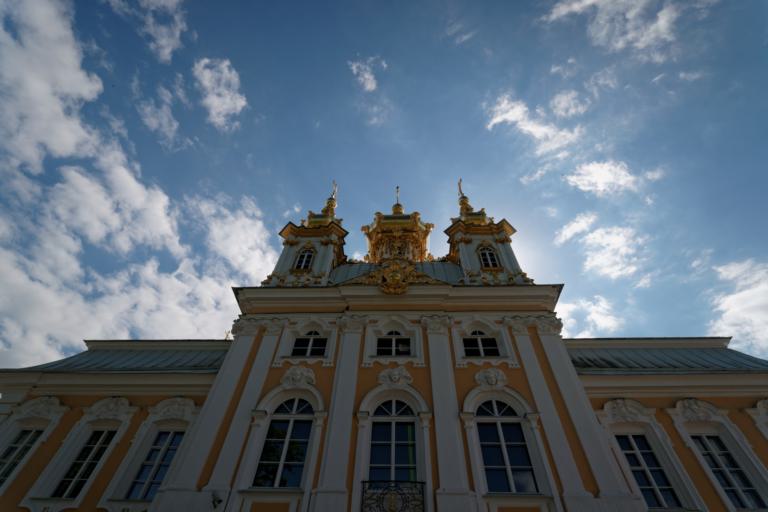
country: RU
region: St.-Petersburg
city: Peterhof
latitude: 59.8845
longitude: 29.9111
